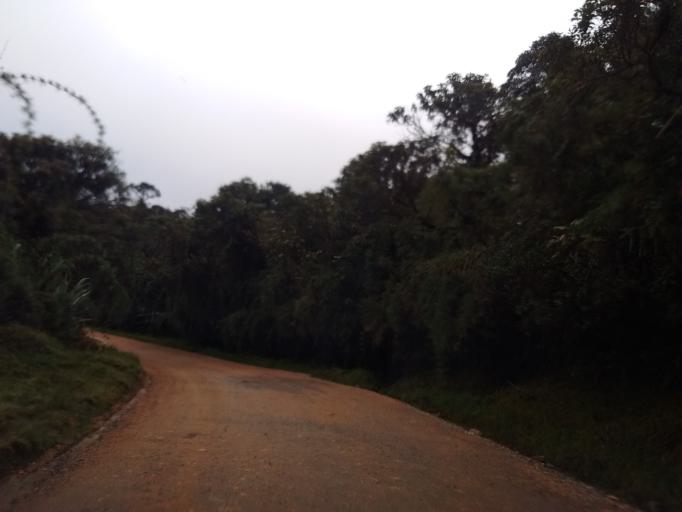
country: CO
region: Huila
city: Isnos
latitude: 2.1280
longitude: -76.3780
